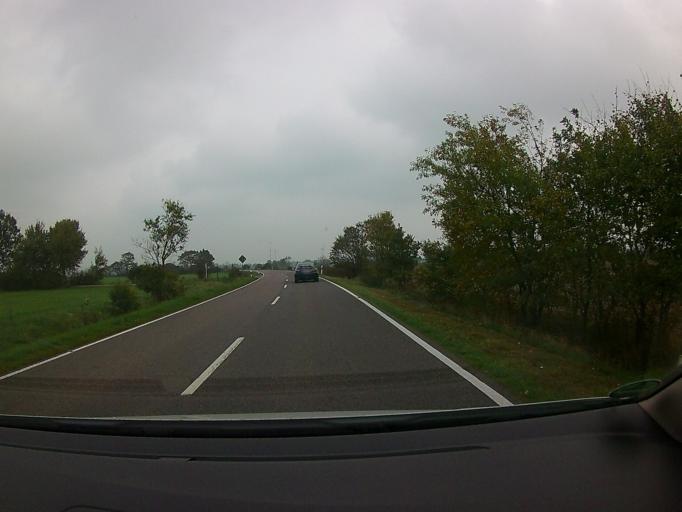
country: DE
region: Schleswig-Holstein
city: Goldebek
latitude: 54.6755
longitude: 9.1590
